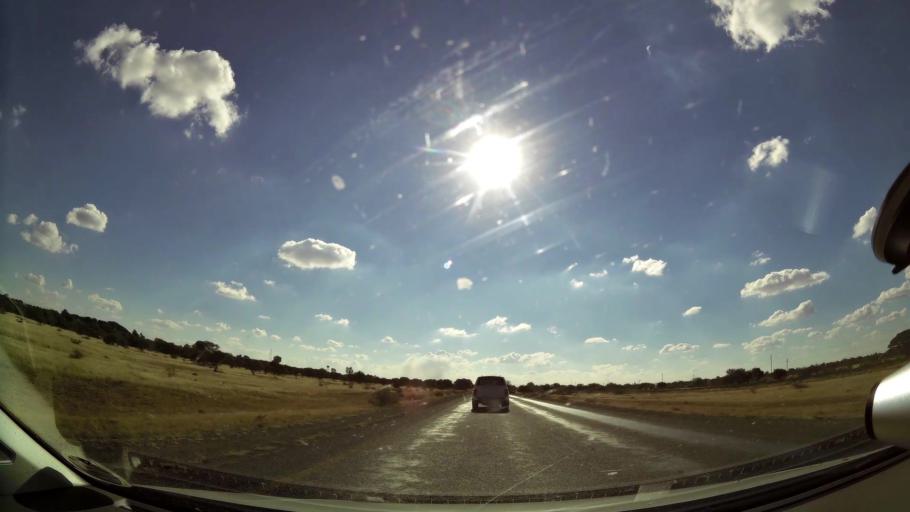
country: ZA
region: Northern Cape
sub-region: Frances Baard District Municipality
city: Kimberley
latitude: -28.7943
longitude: 24.7878
